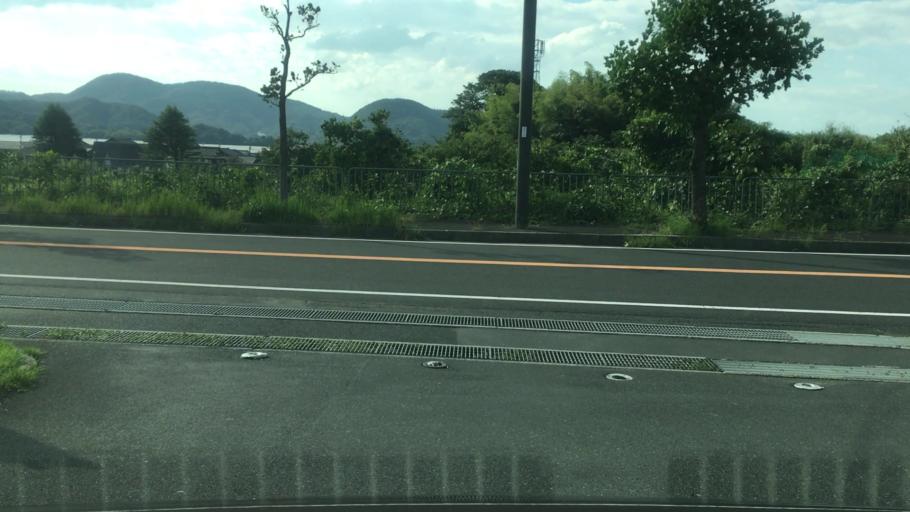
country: JP
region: Hyogo
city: Toyooka
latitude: 35.6304
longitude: 134.9312
